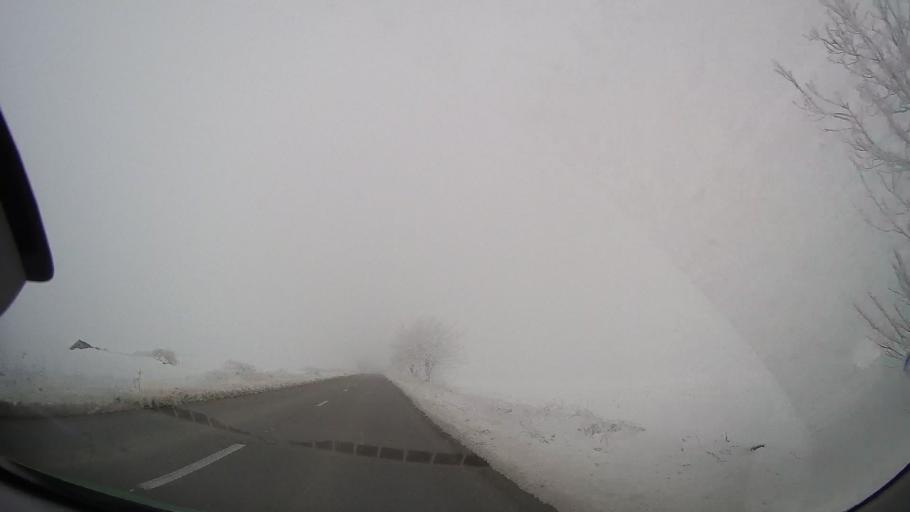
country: RO
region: Iasi
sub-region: Comuna Mogosesti-Siret
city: Mogosesti-Siret
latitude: 47.1500
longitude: 26.7778
